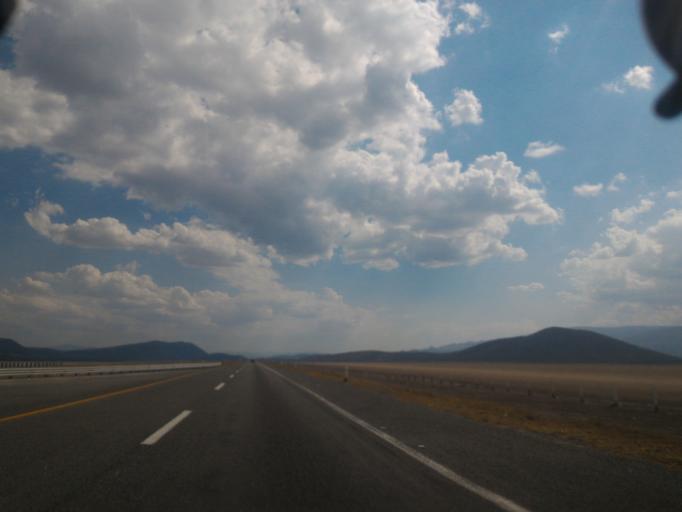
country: MX
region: Jalisco
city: Zacoalco de Torres
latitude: 20.2948
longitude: -103.5568
